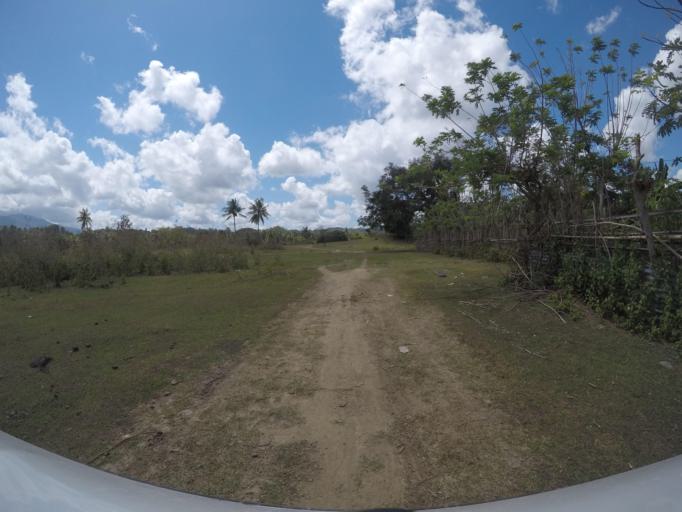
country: TL
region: Viqueque
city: Viqueque
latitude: -8.8401
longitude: 126.3719
